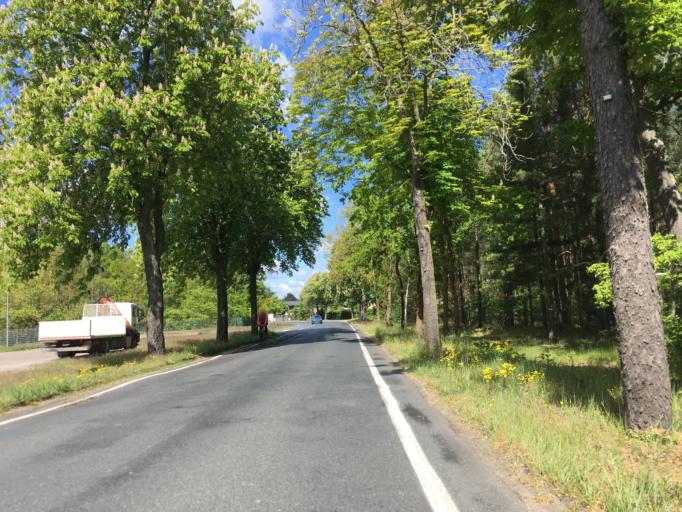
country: DE
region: Brandenburg
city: Oranienburg
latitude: 52.7413
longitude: 13.2714
